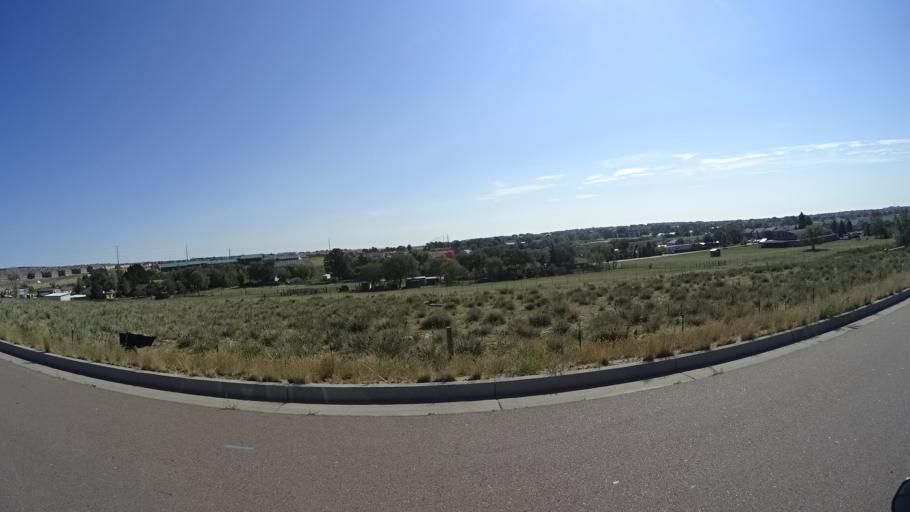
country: US
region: Colorado
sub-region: El Paso County
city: Black Forest
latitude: 38.9378
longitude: -104.6970
